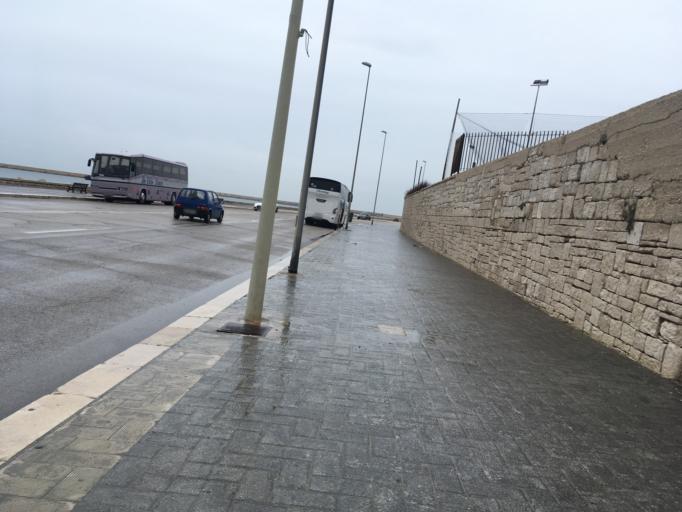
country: IT
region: Apulia
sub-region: Provincia di Bari
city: Bari
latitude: 41.1392
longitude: 16.8433
